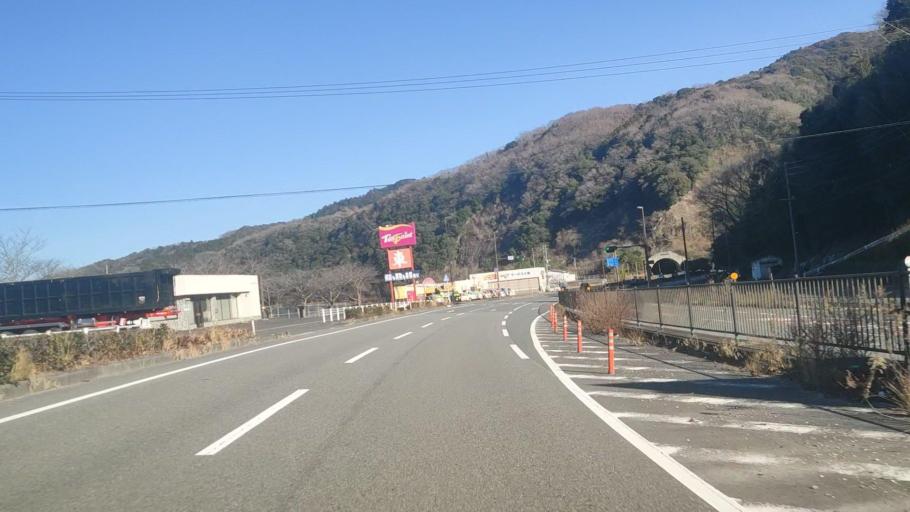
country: JP
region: Oita
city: Oita
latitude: 33.0907
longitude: 131.6432
